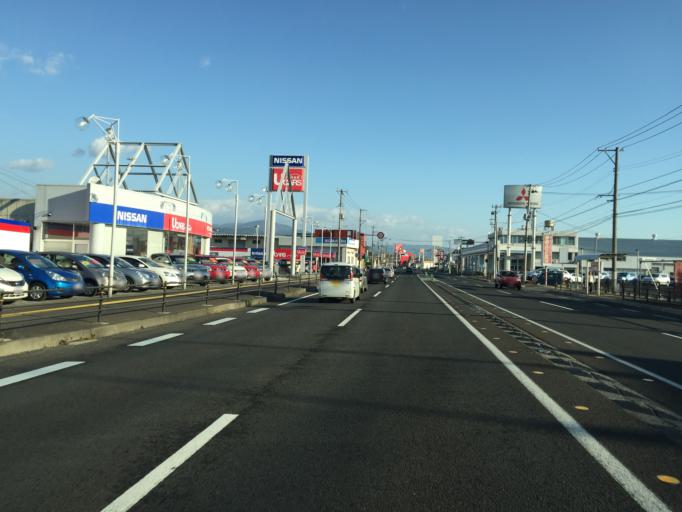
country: JP
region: Fukushima
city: Fukushima-shi
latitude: 37.7807
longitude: 140.4861
